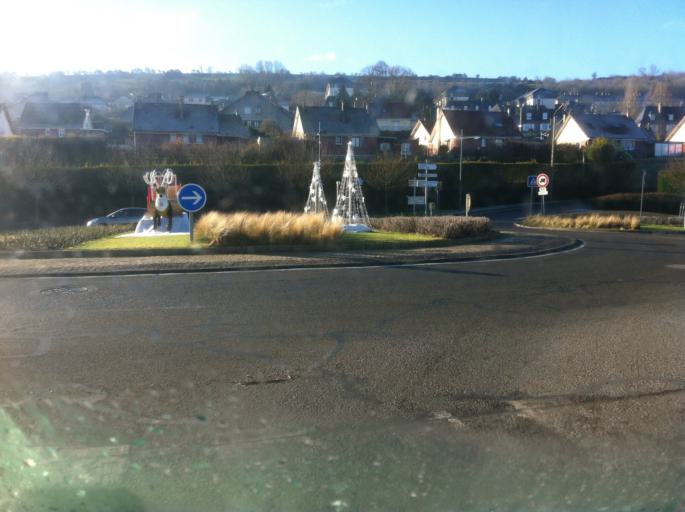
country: FR
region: Picardie
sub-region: Departement de la Somme
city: Mers-les-Bains
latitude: 50.0566
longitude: 1.3871
